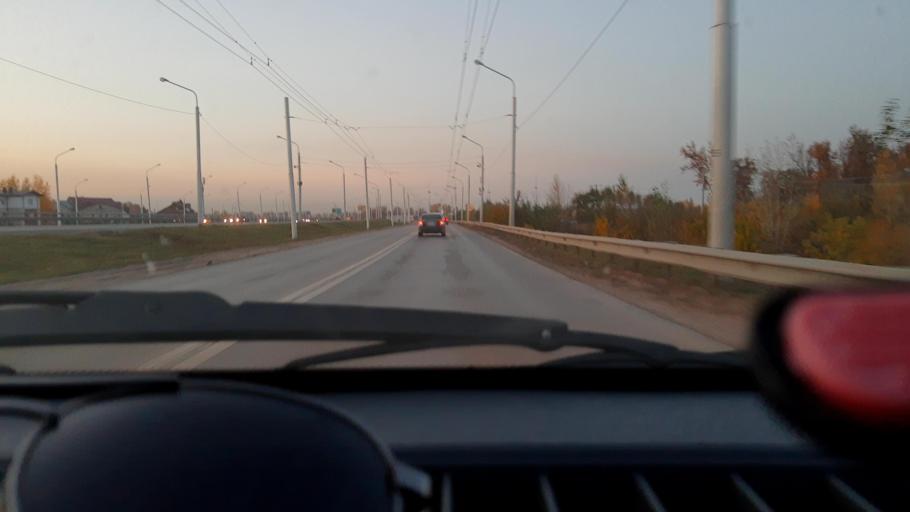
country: RU
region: Bashkortostan
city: Ufa
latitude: 54.7704
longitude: 55.9550
